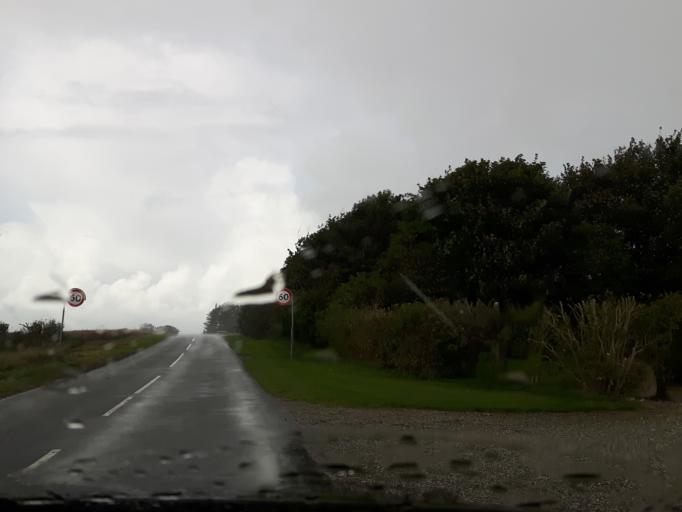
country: DK
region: North Denmark
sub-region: Thisted Kommune
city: Hanstholm
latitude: 57.1009
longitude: 8.6479
